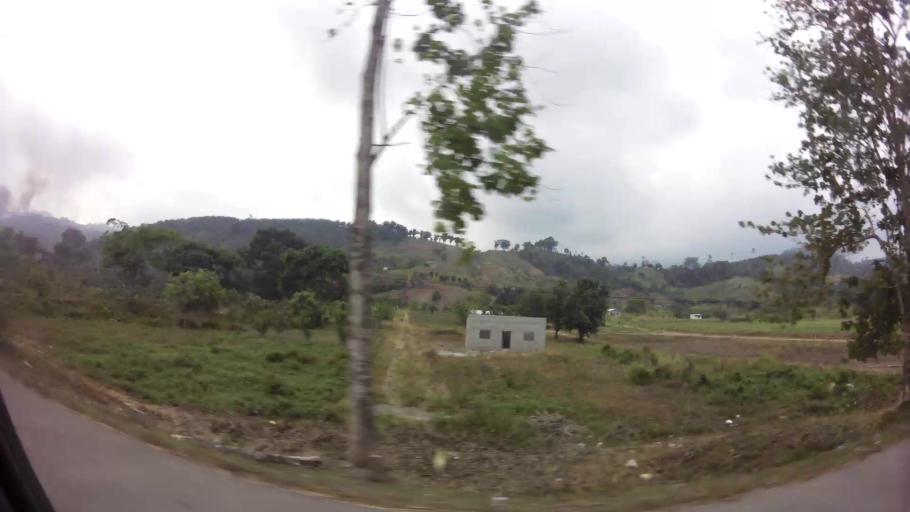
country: HN
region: Yoro
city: Guaimitas
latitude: 15.4980
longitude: -87.7112
